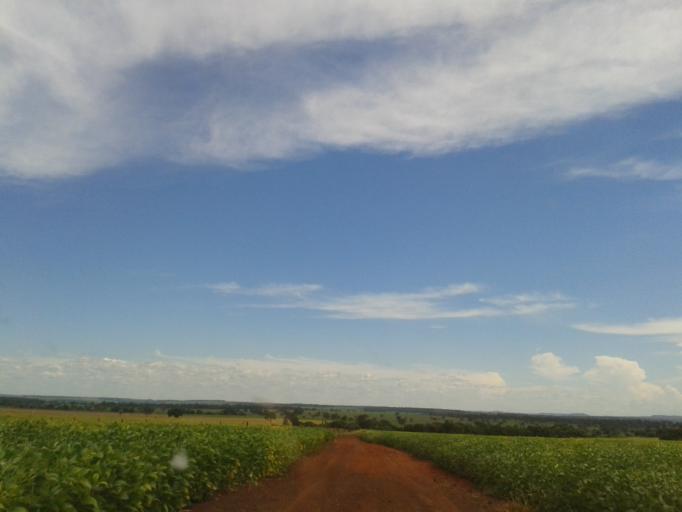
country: BR
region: Minas Gerais
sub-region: Capinopolis
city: Capinopolis
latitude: -18.7689
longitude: -49.7967
